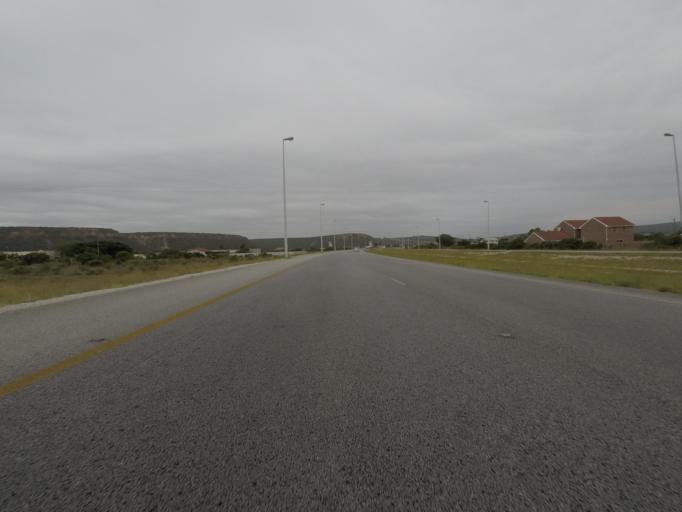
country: ZA
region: Eastern Cape
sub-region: Nelson Mandela Bay Metropolitan Municipality
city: Port Elizabeth
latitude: -33.6931
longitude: 25.8161
